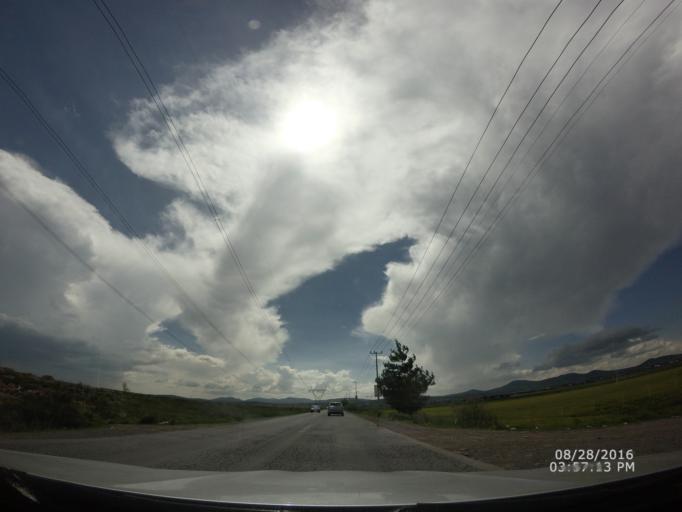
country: MX
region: Hidalgo
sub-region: Mineral de la Reforma
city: Forjadores de Pachuca
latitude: 20.0354
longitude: -98.7648
